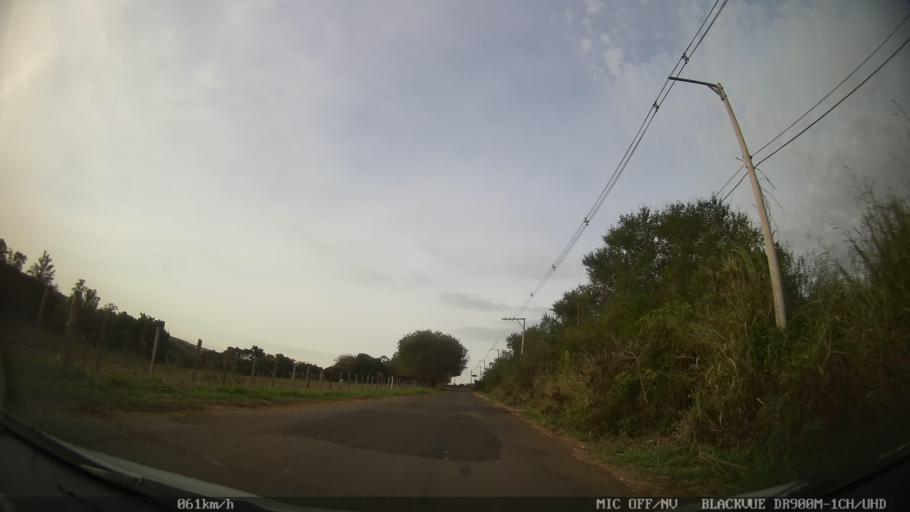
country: BR
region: Sao Paulo
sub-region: Piracicaba
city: Piracicaba
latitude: -22.6948
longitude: -47.5847
